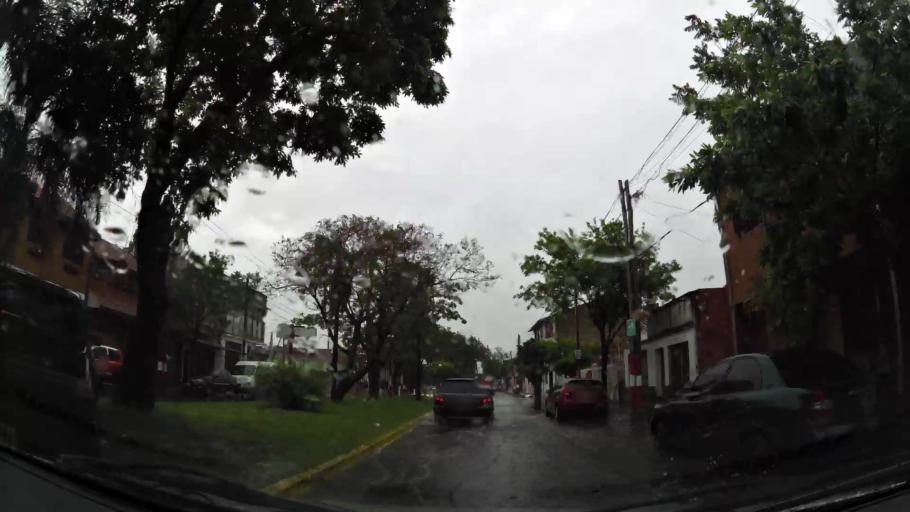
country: AR
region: Buenos Aires
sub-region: Partido de Lanus
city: Lanus
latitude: -34.7231
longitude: -58.4020
